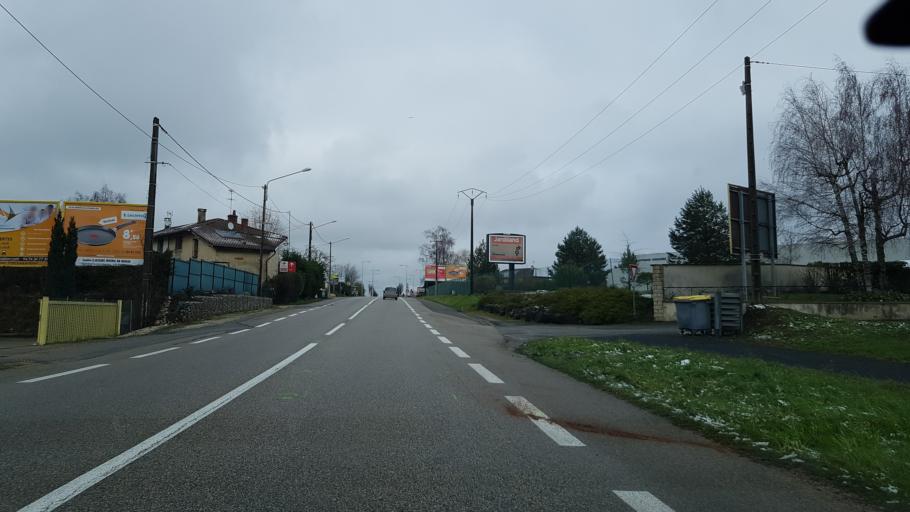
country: FR
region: Rhone-Alpes
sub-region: Departement de l'Ain
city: Peronnas
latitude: 46.1736
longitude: 5.1987
